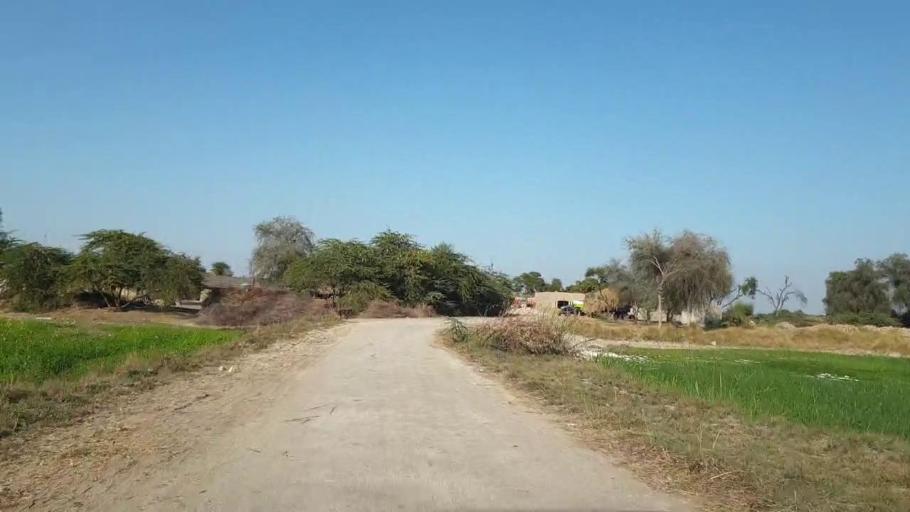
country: PK
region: Sindh
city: Khadro
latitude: 26.1910
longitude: 68.7658
